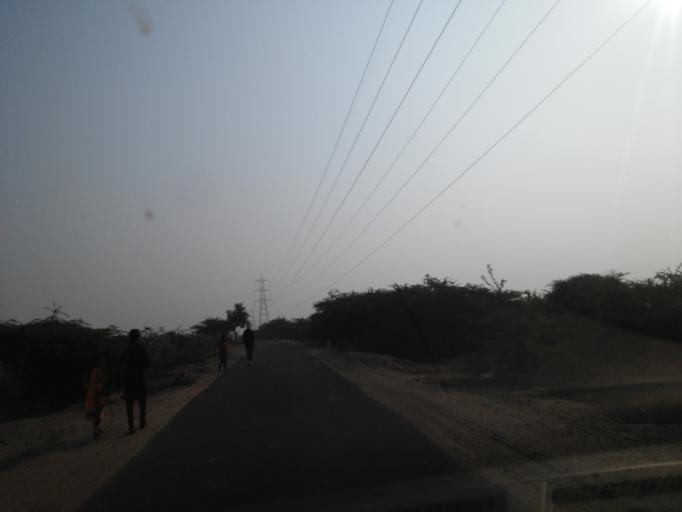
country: IN
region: Gujarat
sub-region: Kachchh
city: Mandvi
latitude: 22.8325
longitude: 69.5066
